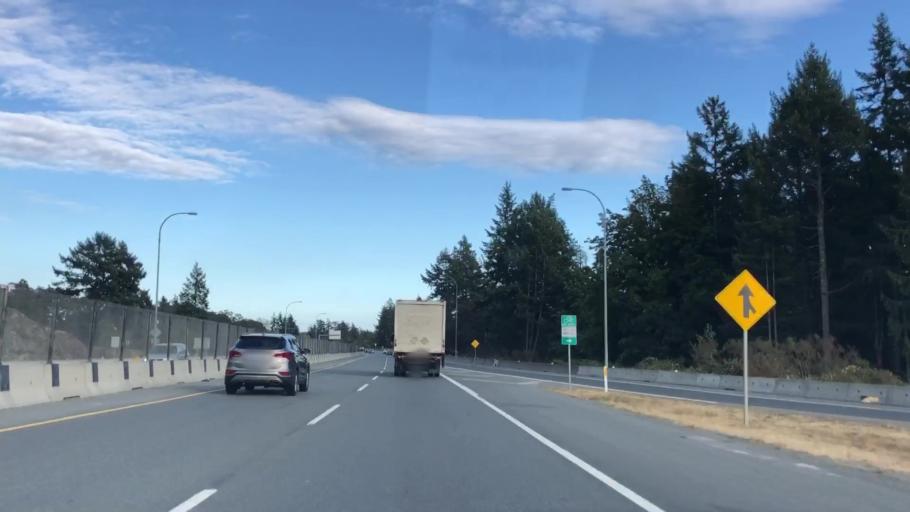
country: CA
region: British Columbia
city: Langford
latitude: 48.4541
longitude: -123.5169
